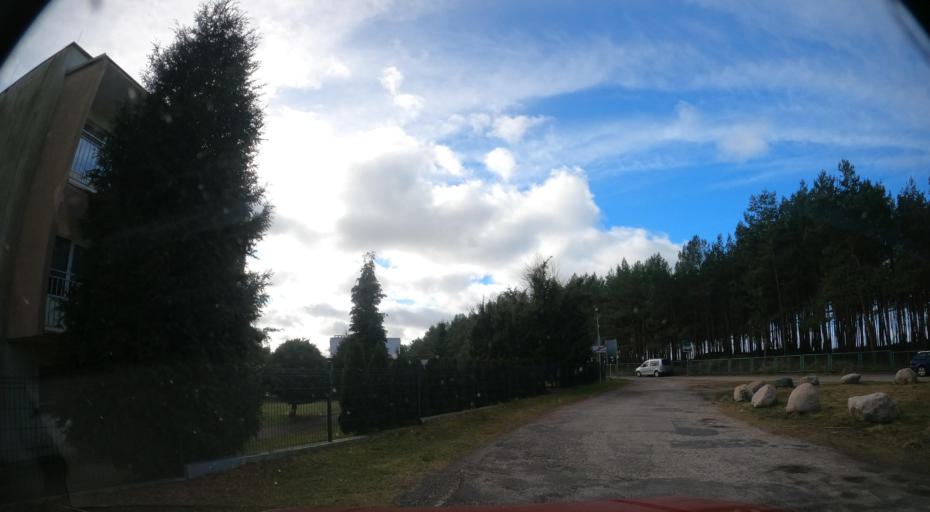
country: PL
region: West Pomeranian Voivodeship
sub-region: Powiat koszalinski
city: Sianow
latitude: 54.3152
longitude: 16.2078
